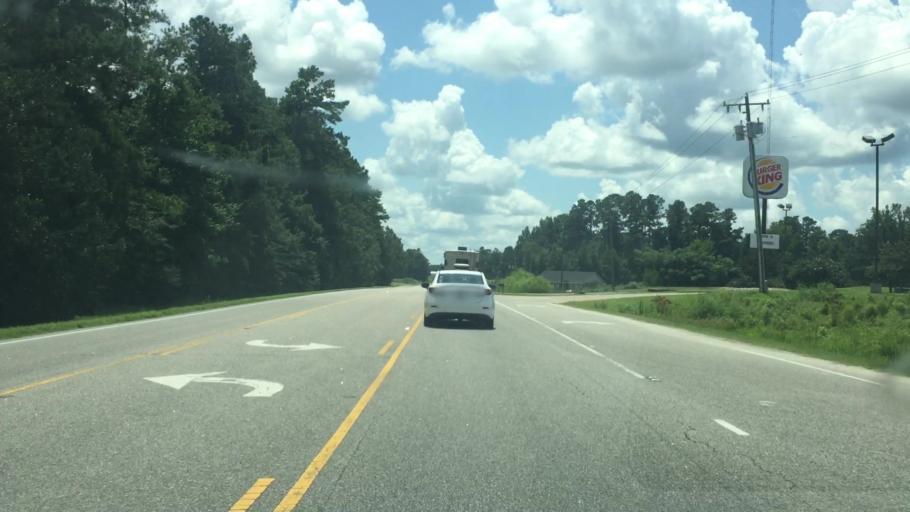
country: US
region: North Carolina
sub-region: Columbus County
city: Tabor City
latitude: 34.1550
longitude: -78.8591
